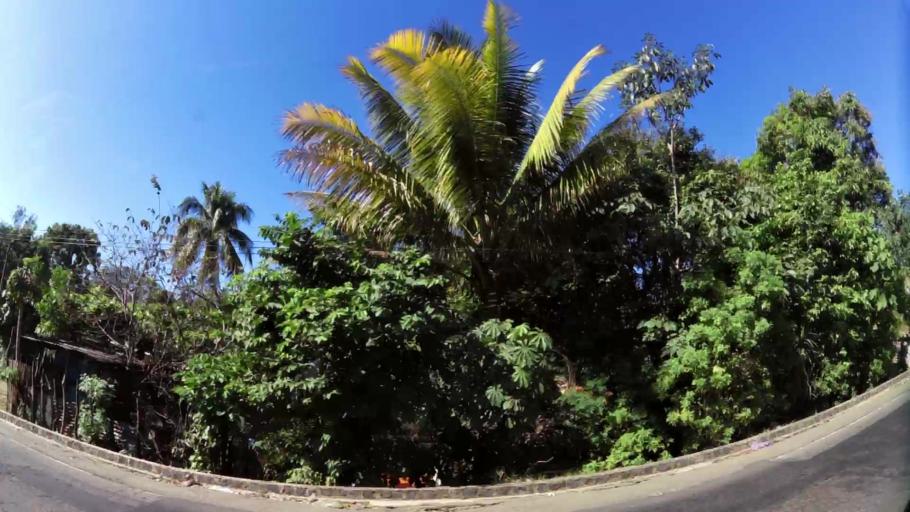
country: SV
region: Sonsonate
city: Sonsonate
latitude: 13.7314
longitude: -89.7315
